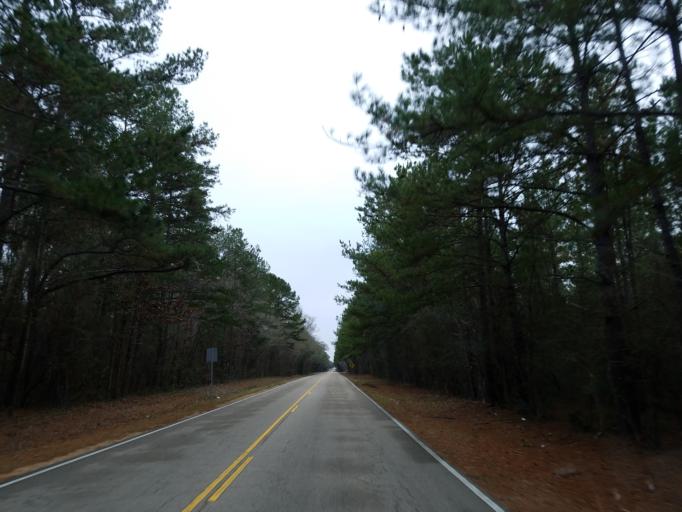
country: US
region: Mississippi
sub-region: Forrest County
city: Hattiesburg
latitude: 31.2560
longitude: -89.2340
